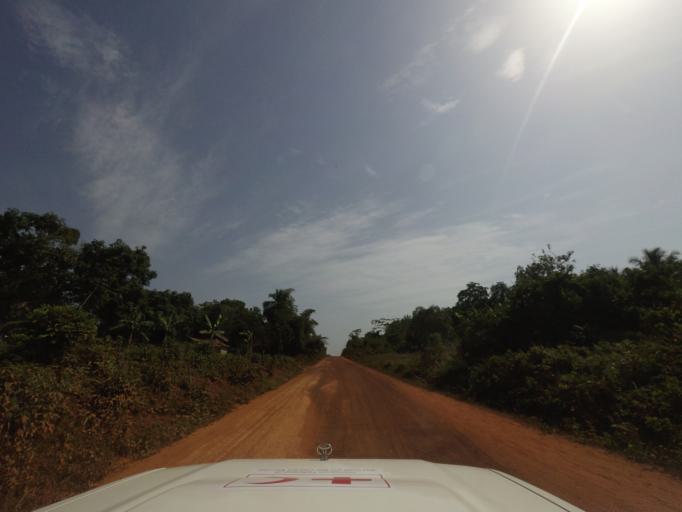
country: LR
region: Bong
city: Gbarnga
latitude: 7.0532
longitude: -9.4679
